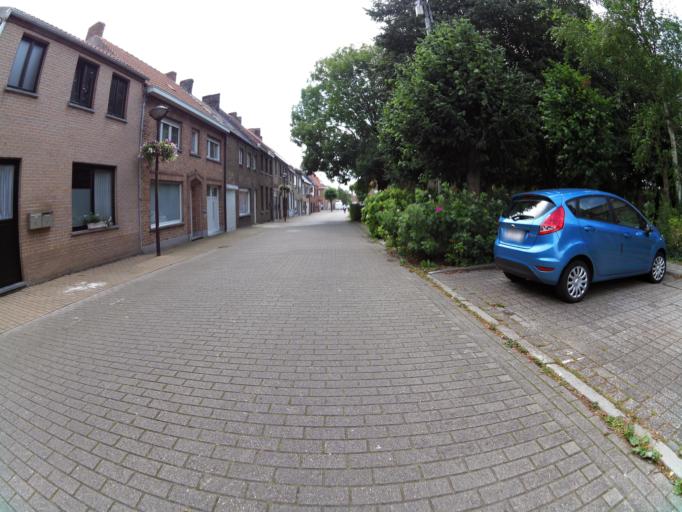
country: BE
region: Flanders
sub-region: Provincie West-Vlaanderen
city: Oudenburg
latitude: 51.1841
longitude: 3.0038
